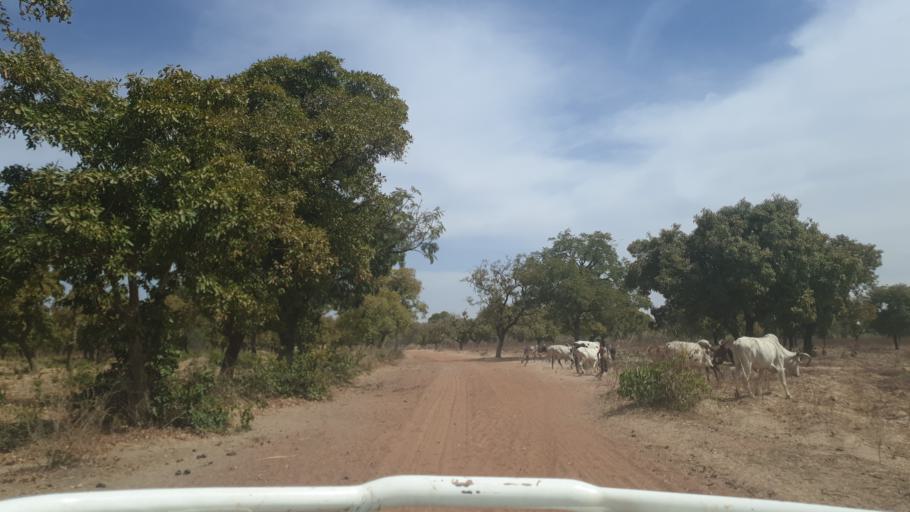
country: ML
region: Sikasso
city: Yorosso
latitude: 12.2733
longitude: -4.6927
